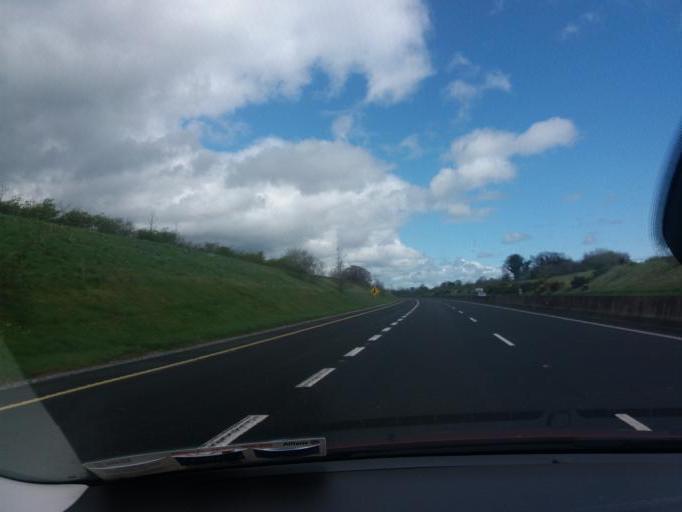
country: IE
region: Munster
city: Thurles
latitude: 52.6262
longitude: -7.7702
